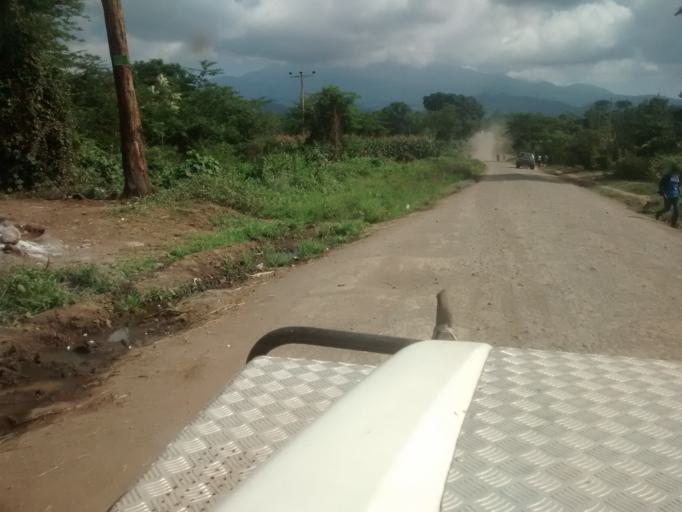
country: TZ
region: Arusha
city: Usa River
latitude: -3.3689
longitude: 36.8469
